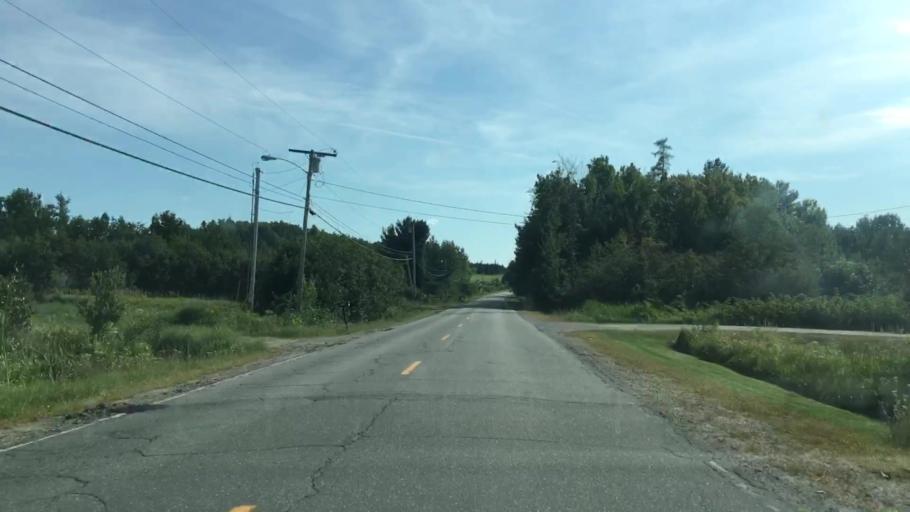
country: US
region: Maine
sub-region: Penobscot County
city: Lincoln
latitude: 45.3244
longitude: -68.5326
